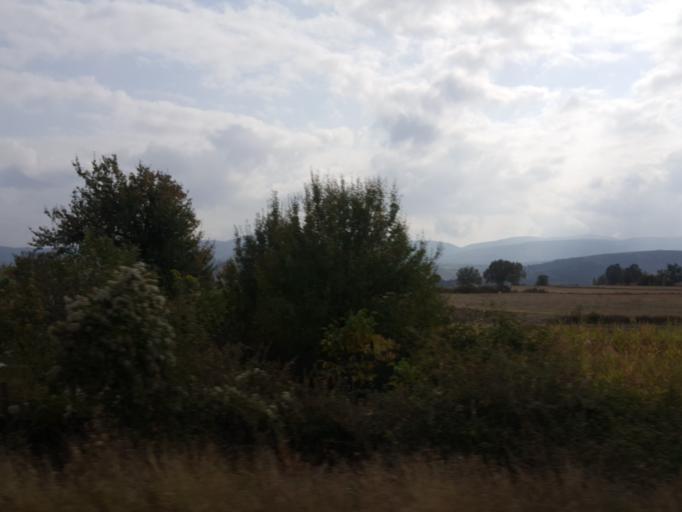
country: TR
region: Sinop
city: Sarayduzu
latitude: 41.3314
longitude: 34.7742
